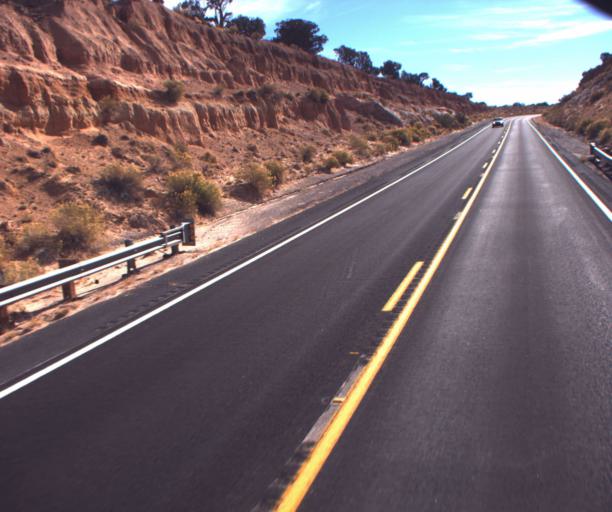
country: US
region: Arizona
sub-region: Coconino County
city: Kaibito
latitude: 36.6020
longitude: -110.9164
